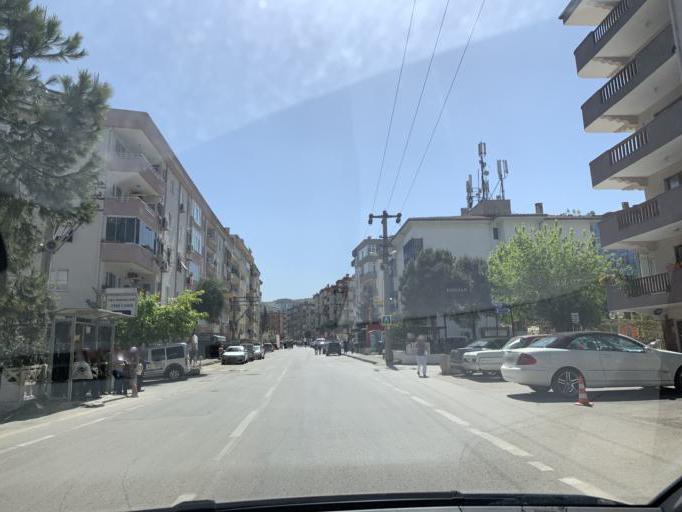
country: TR
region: Bursa
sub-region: Mudanya
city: Mudanya
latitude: 40.3552
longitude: 28.9235
